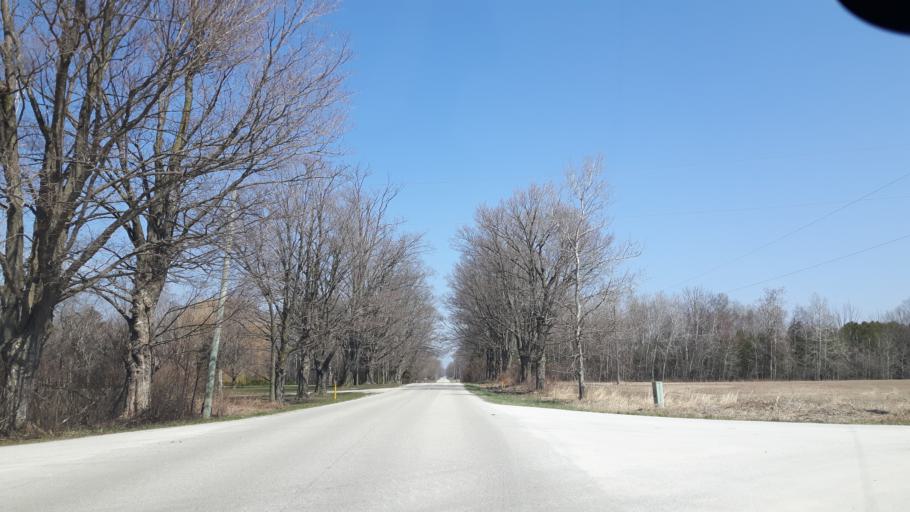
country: CA
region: Ontario
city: Goderich
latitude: 43.6241
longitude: -81.6846
